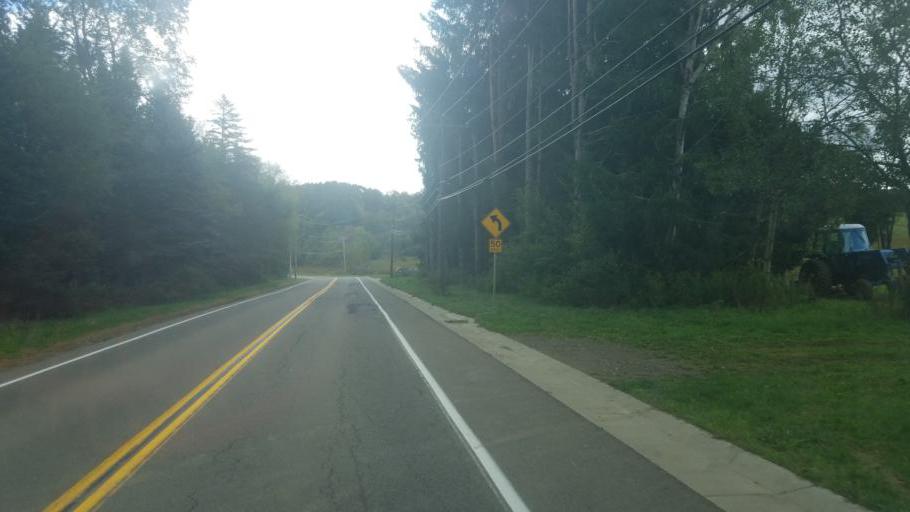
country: US
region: New York
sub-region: Cattaraugus County
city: Weston Mills
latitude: 42.0892
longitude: -78.3596
